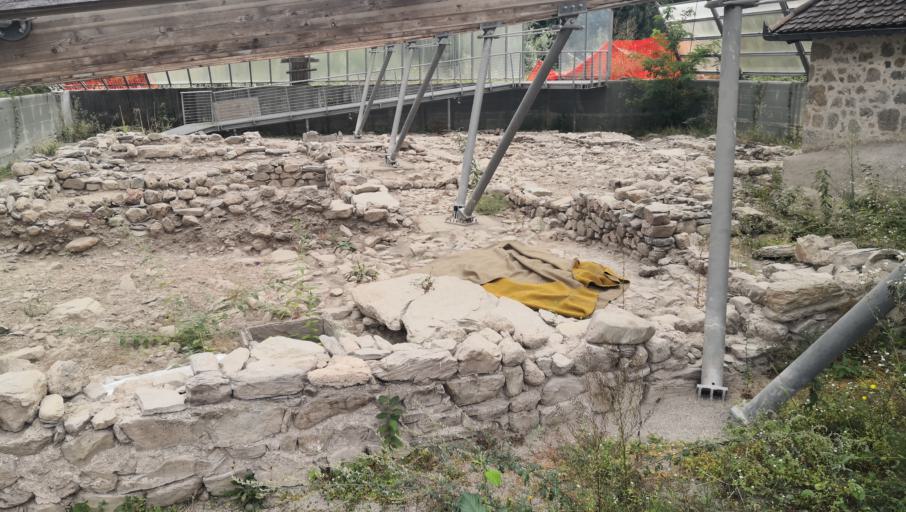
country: IT
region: Friuli Venezia Giulia
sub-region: Provincia di Udine
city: Ovaro
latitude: 46.4881
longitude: 12.8620
